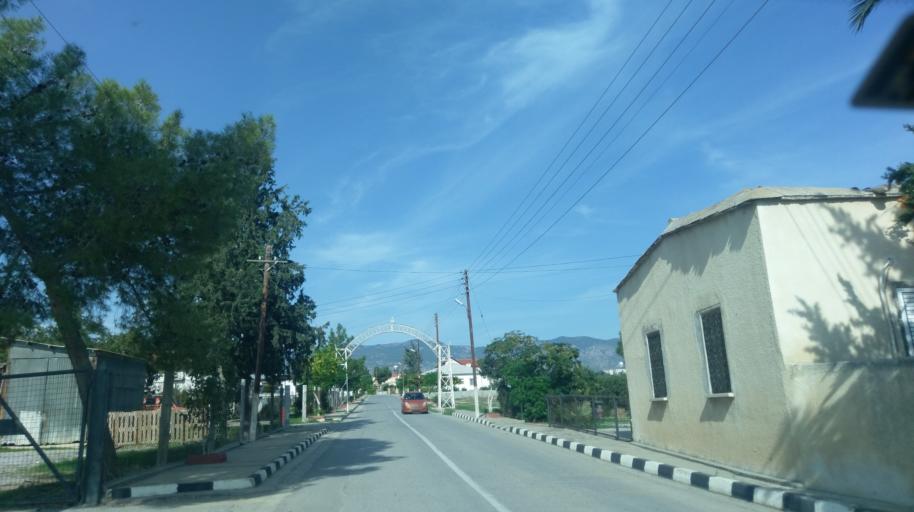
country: CY
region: Ammochostos
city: Lefkonoiko
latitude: 35.2464
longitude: 33.6077
